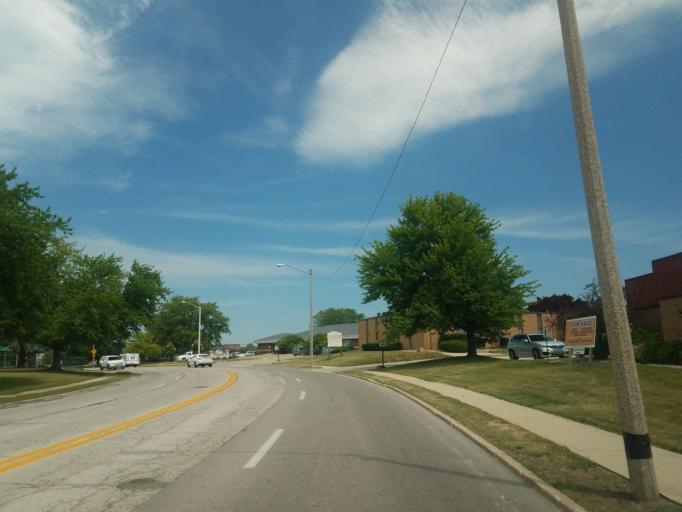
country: US
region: Illinois
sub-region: McLean County
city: Bloomington
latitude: 40.4812
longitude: -88.9593
